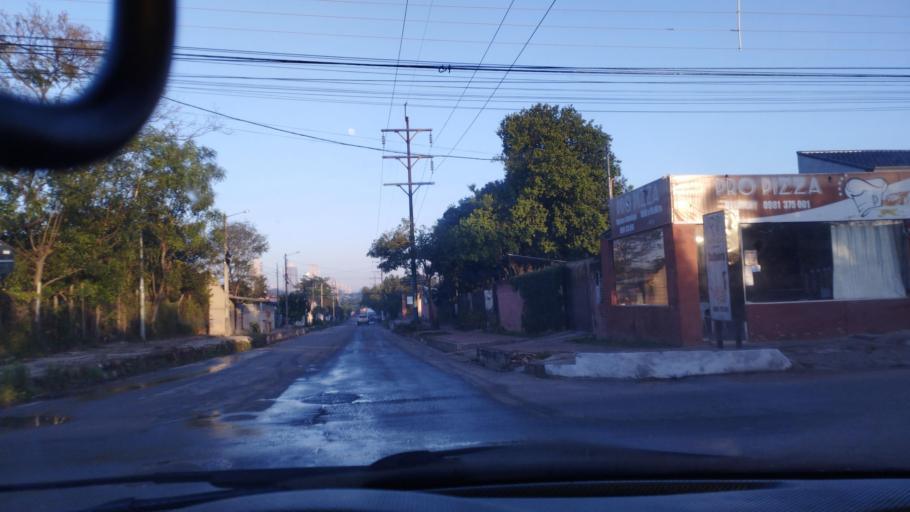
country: PY
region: Central
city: Fernando de la Mora
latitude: -25.2945
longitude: -57.5394
